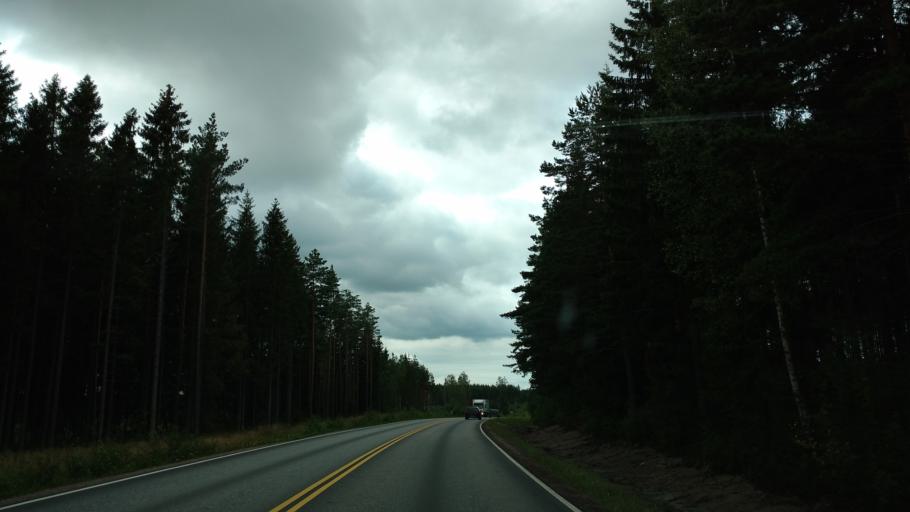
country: FI
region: Varsinais-Suomi
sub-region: Aboland-Turunmaa
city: Vaestanfjaerd
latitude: 60.1165
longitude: 22.6185
